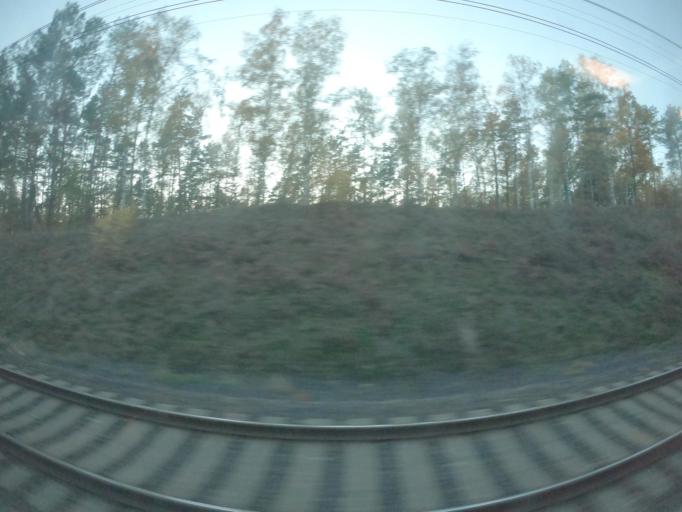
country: PL
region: West Pomeranian Voivodeship
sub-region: Powiat mysliborski
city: Boleszkowice
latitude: 52.7160
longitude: 14.5321
